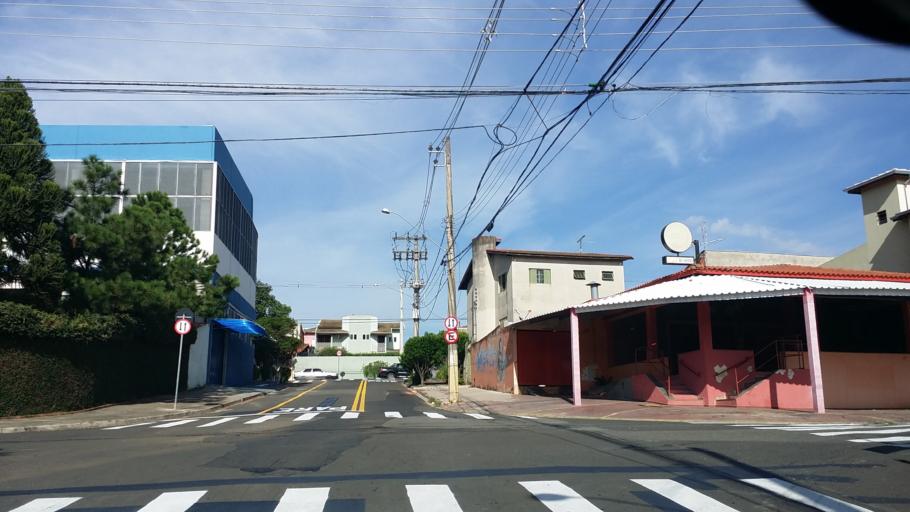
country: BR
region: Sao Paulo
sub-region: Indaiatuba
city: Indaiatuba
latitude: -23.0984
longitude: -47.2295
